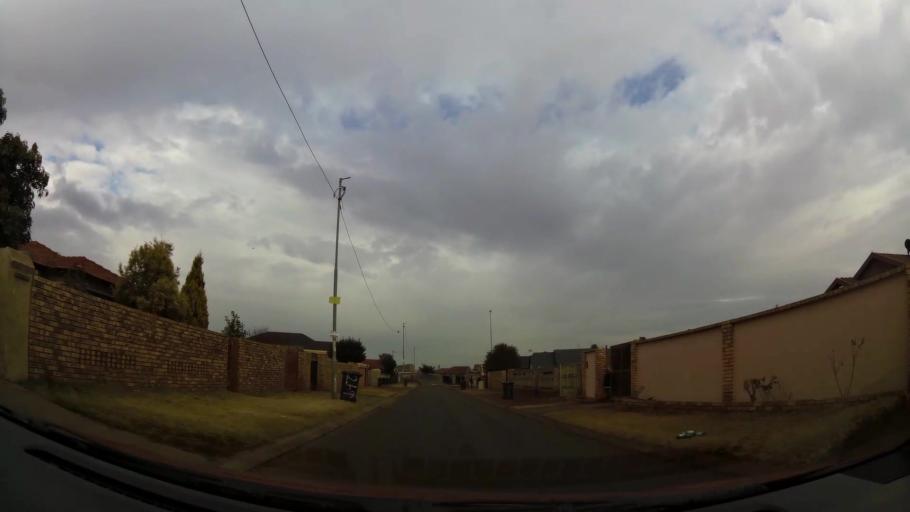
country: ZA
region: Gauteng
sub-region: City of Johannesburg Metropolitan Municipality
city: Soweto
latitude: -26.2822
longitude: 27.8379
